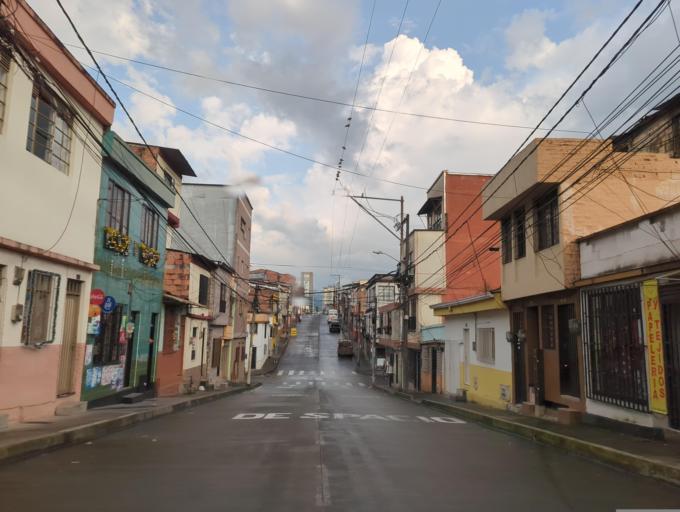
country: CO
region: Risaralda
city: Pereira
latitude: 4.8132
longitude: -75.7033
